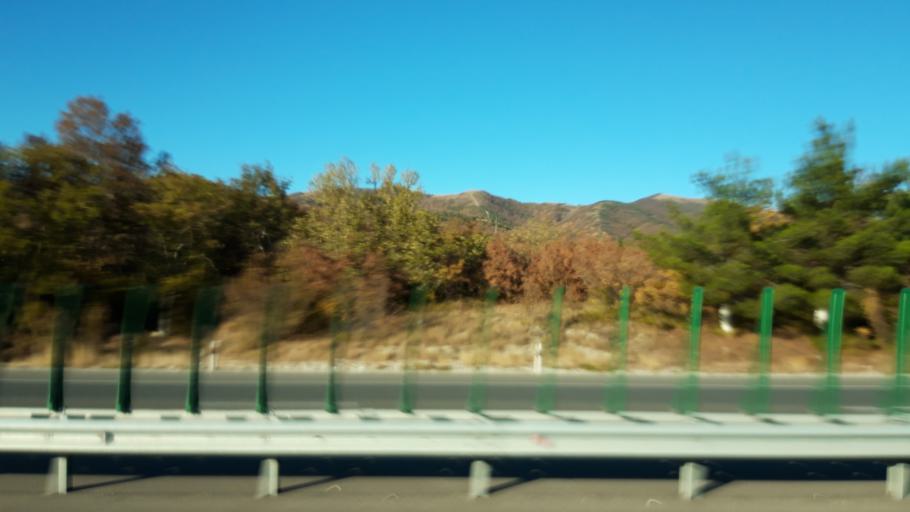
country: RU
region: Krasnodarskiy
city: Kabardinka
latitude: 44.6410
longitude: 37.9784
